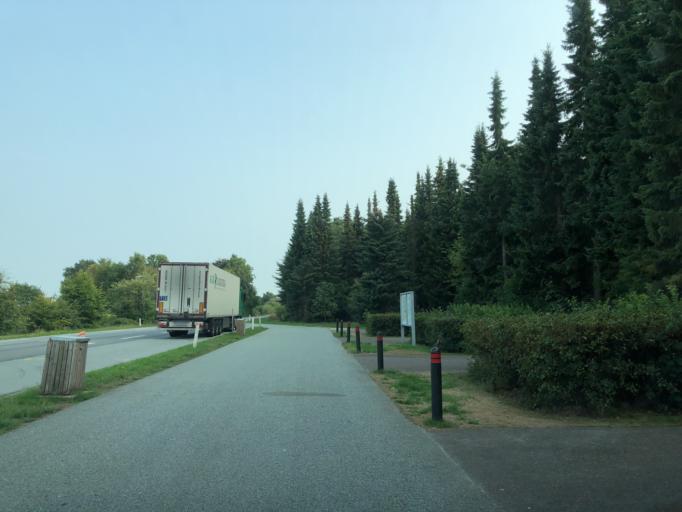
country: DK
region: Central Jutland
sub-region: Herning Kommune
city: Kibaek
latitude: 55.9214
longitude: 8.7922
